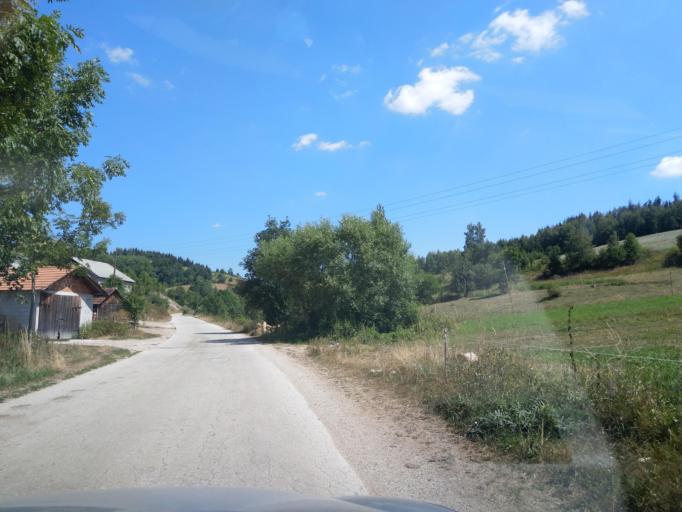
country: RS
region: Central Serbia
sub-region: Zlatiborski Okrug
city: Nova Varos
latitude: 43.4546
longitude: 19.9714
